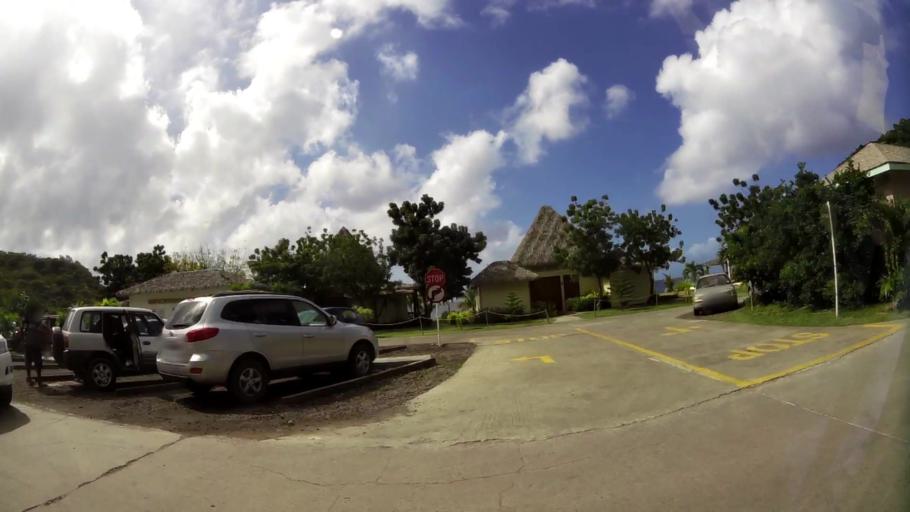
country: MS
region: Saint Peter
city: Brades
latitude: 16.8021
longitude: -62.2048
